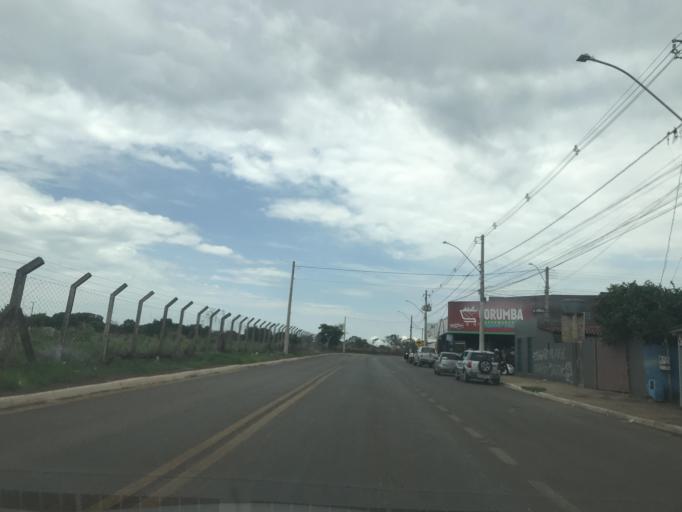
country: BR
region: Goias
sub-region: Luziania
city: Luziania
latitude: -16.2570
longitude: -47.9655
